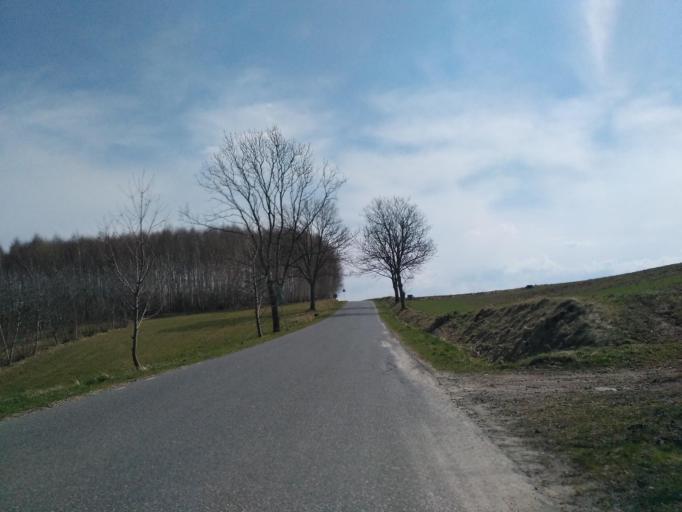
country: PL
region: Subcarpathian Voivodeship
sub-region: Powiat ropczycko-sedziszowski
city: Iwierzyce
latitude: 49.9859
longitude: 21.7341
